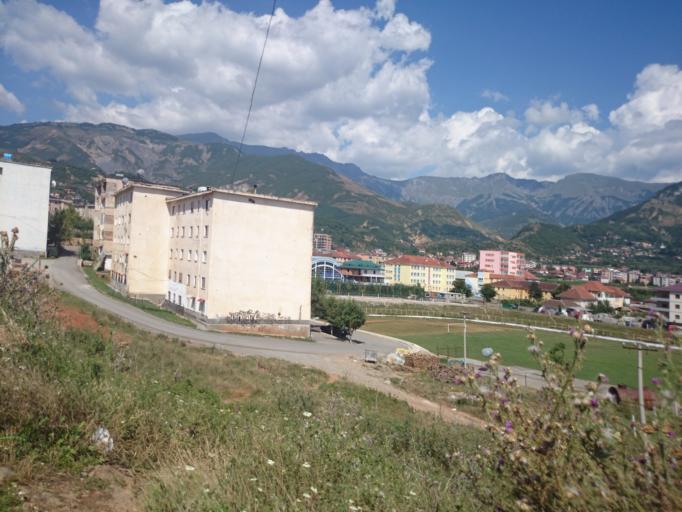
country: AL
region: Diber
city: Peshkopi
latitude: 41.6804
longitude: 20.4239
